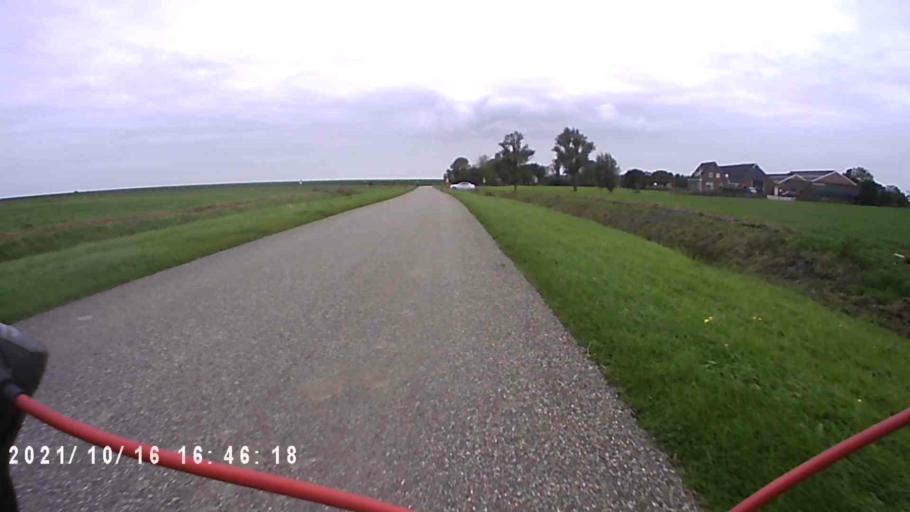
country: NL
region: Friesland
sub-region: Gemeente Dongeradeel
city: Anjum
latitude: 53.3624
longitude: 6.1439
